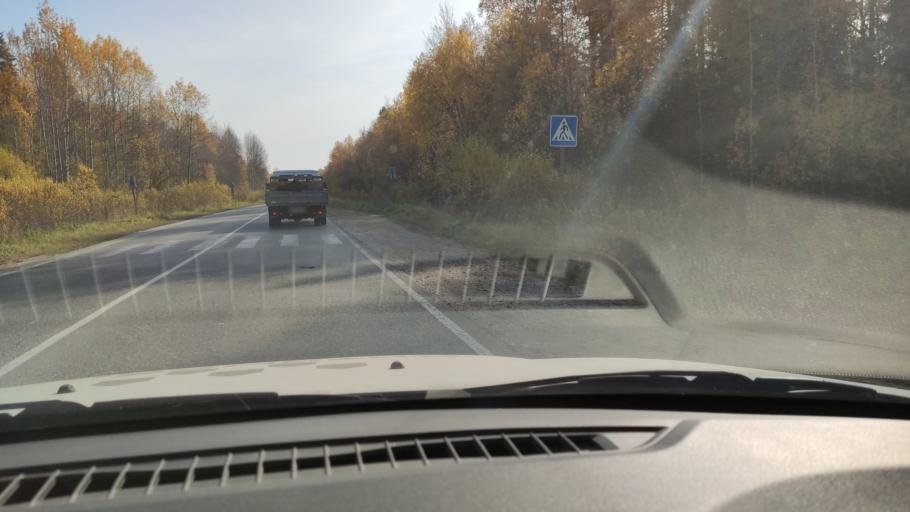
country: RU
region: Perm
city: Novyye Lyady
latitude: 58.0265
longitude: 56.6306
